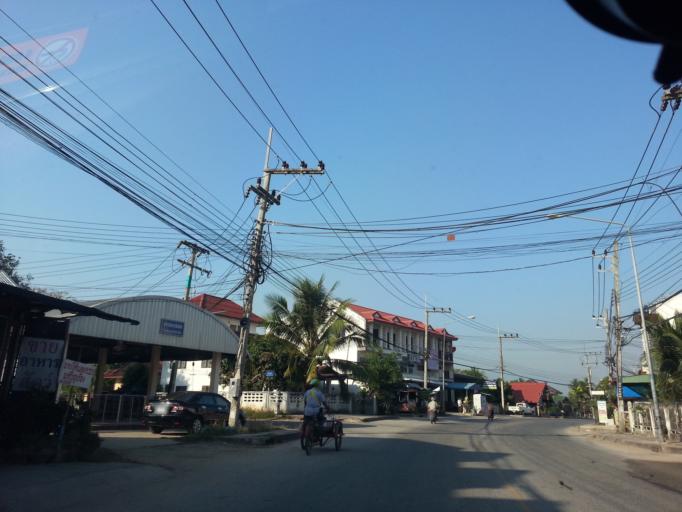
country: TH
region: Chiang Mai
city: San Sai
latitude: 18.8746
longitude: 99.0508
